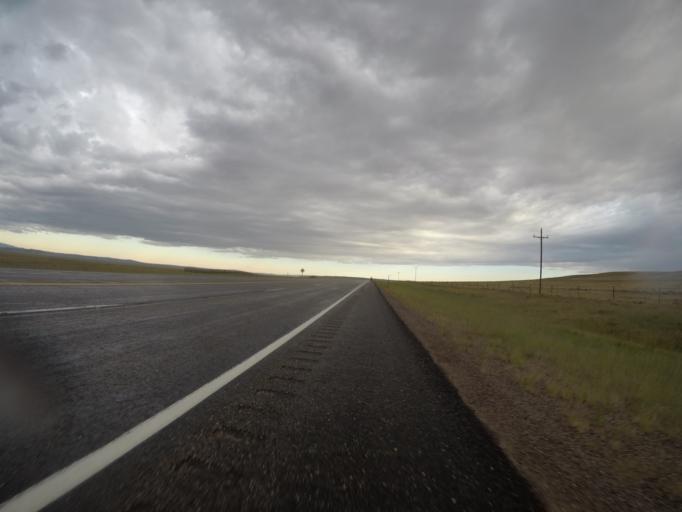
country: US
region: Wyoming
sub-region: Albany County
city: Laramie
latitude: 41.8292
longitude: -106.0124
